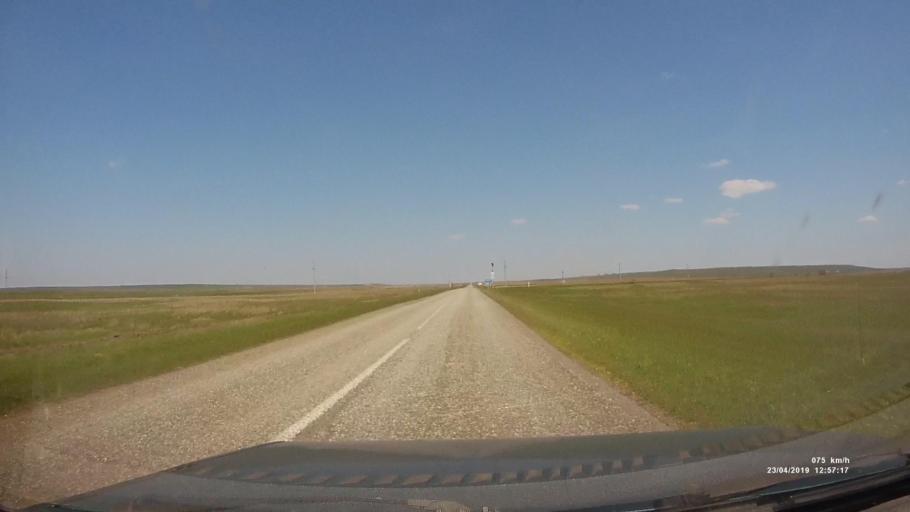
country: RU
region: Kalmykiya
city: Yashalta
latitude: 46.6024
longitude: 42.5798
